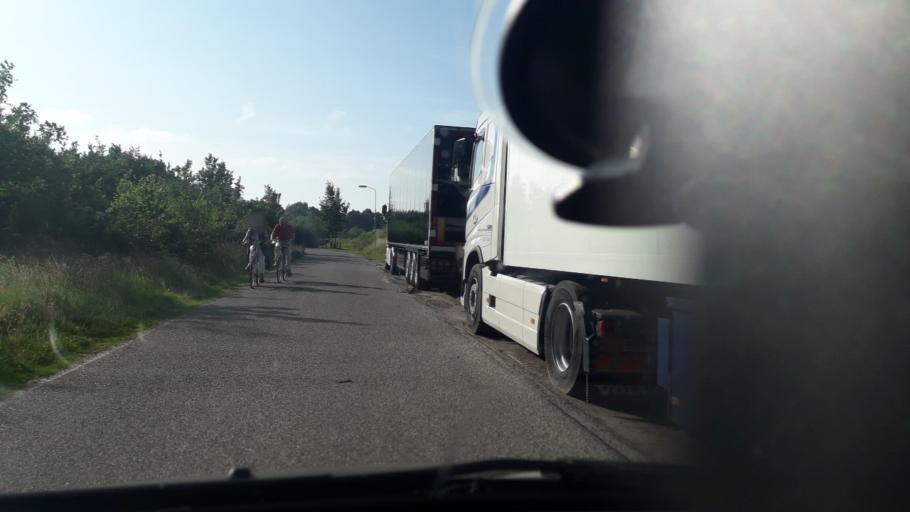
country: NL
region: Gelderland
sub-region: Gemeente Ermelo
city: Horst
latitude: 52.3228
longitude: 5.5810
